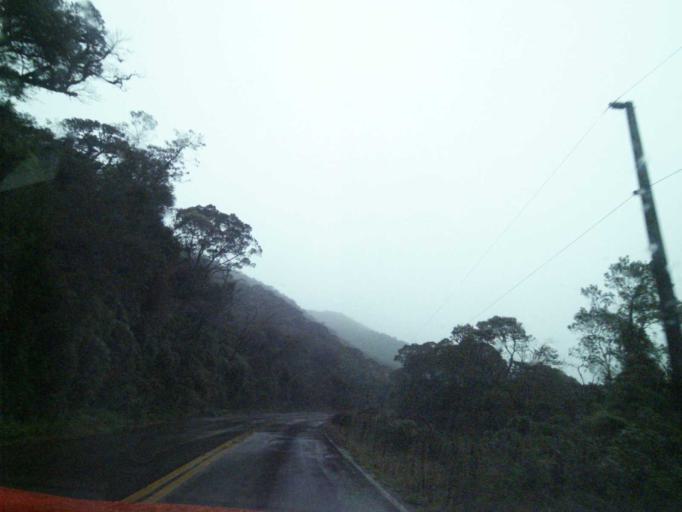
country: BR
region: Santa Catarina
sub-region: Anitapolis
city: Anitapolis
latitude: -27.7536
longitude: -49.0352
